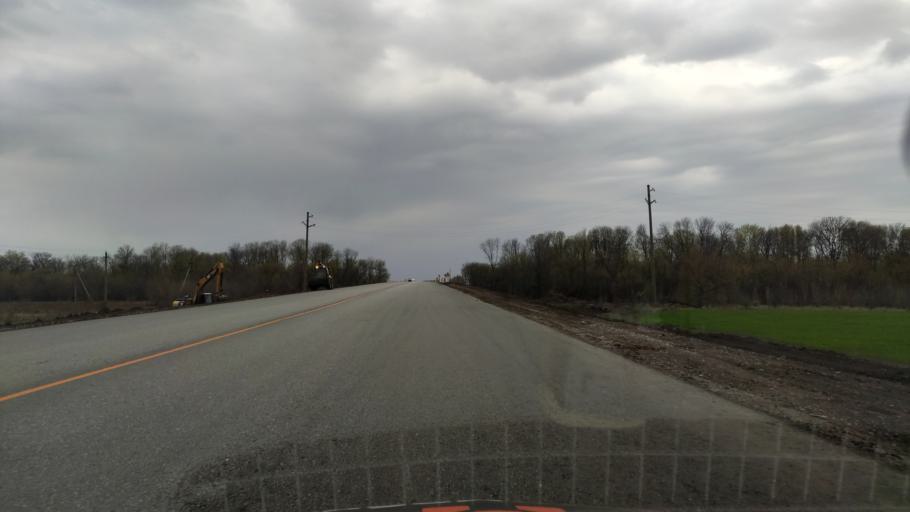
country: RU
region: Kursk
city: Gorshechnoye
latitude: 51.5505
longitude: 38.0431
